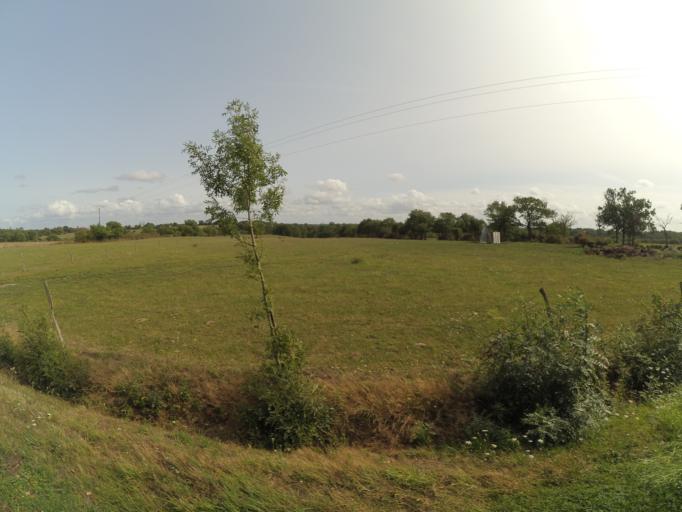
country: FR
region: Pays de la Loire
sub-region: Departement de la Loire-Atlantique
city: Boussay
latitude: 47.0392
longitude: -1.1605
